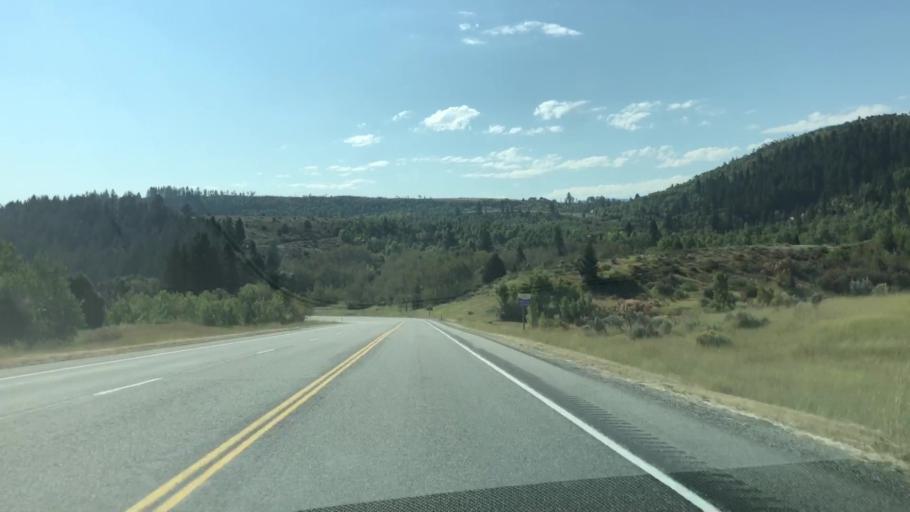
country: US
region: Idaho
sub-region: Teton County
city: Victor
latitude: 43.4529
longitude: -111.4049
